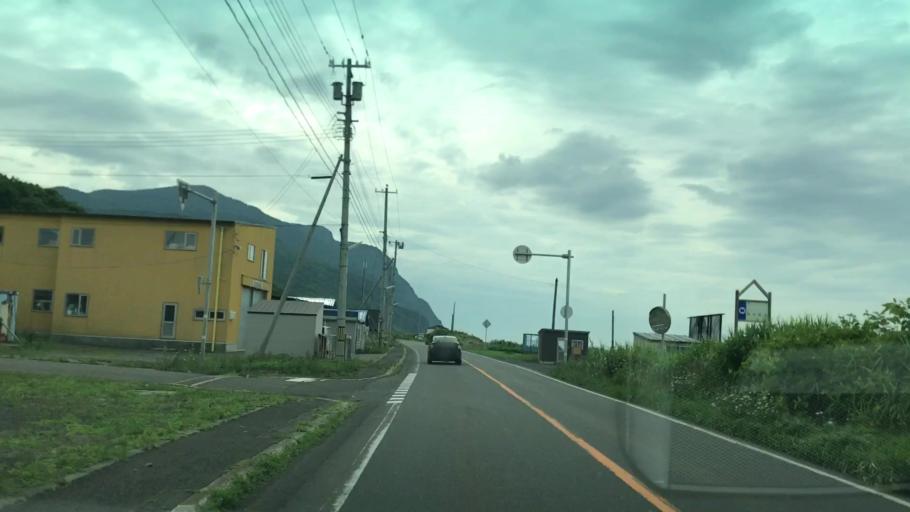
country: JP
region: Hokkaido
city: Iwanai
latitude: 42.9697
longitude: 140.4772
